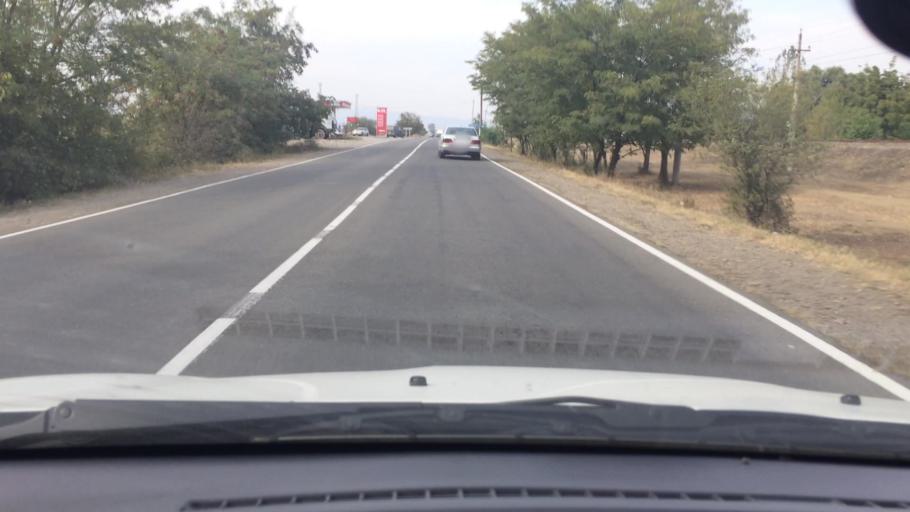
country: GE
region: Kvemo Kartli
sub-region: Marneuli
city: Marneuli
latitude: 41.4286
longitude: 44.8220
